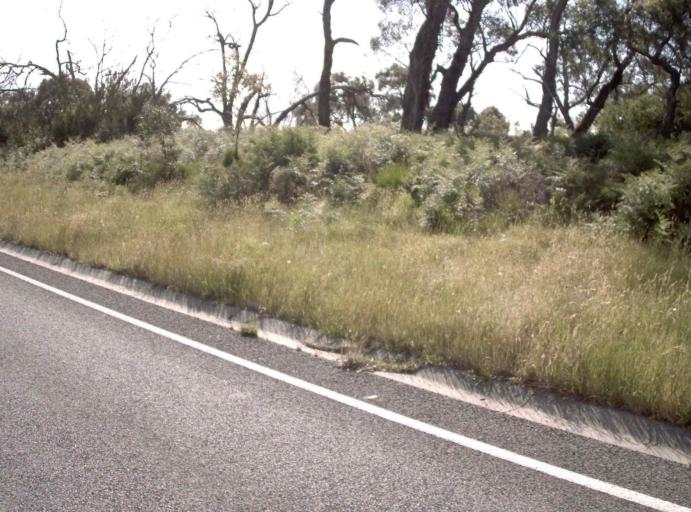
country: AU
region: Victoria
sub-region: Bass Coast
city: North Wonthaggi
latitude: -38.4300
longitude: 145.5036
